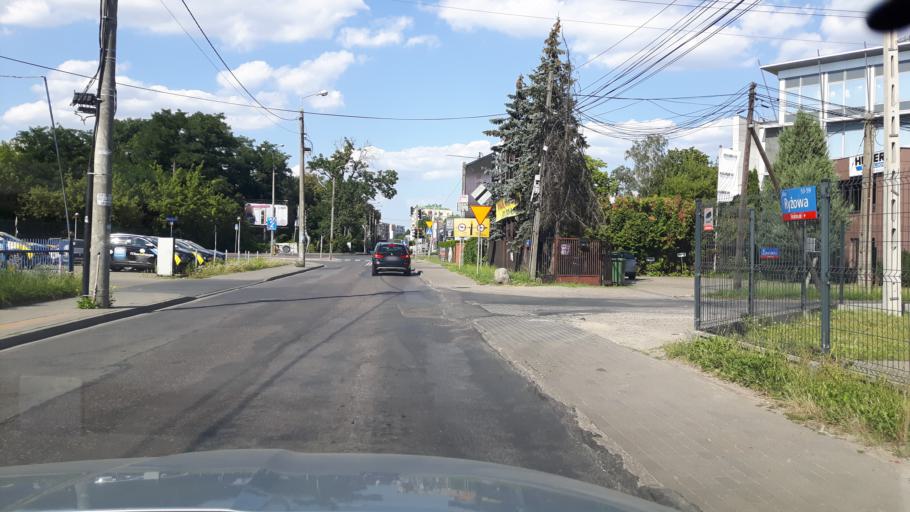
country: PL
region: Masovian Voivodeship
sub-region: Warszawa
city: Ursus
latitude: 52.1850
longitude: 20.9043
